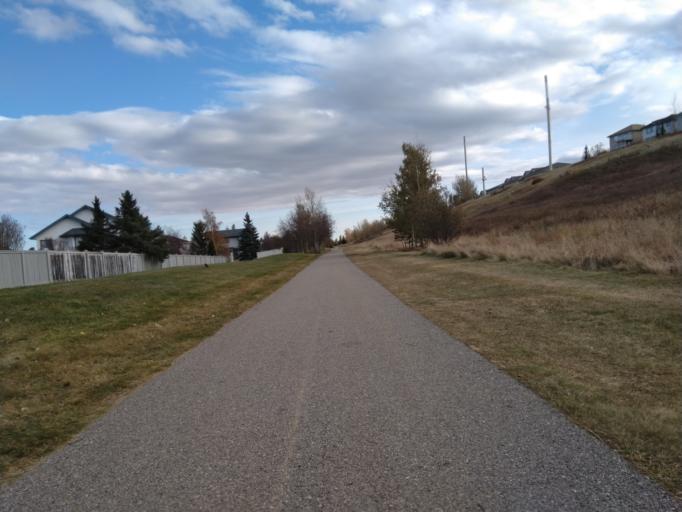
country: CA
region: Alberta
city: Calgary
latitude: 51.1489
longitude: -114.1083
